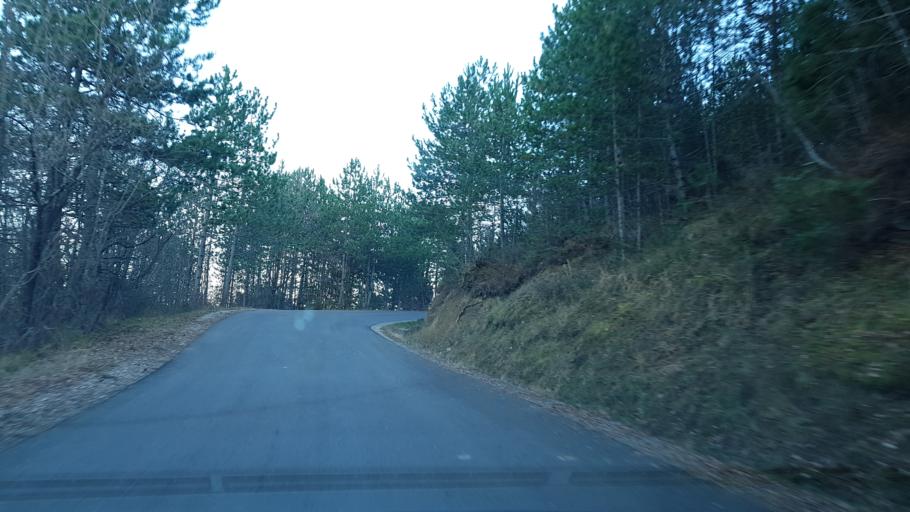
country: SI
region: Koper-Capodistria
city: Pobegi
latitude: 45.4931
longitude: 13.7907
